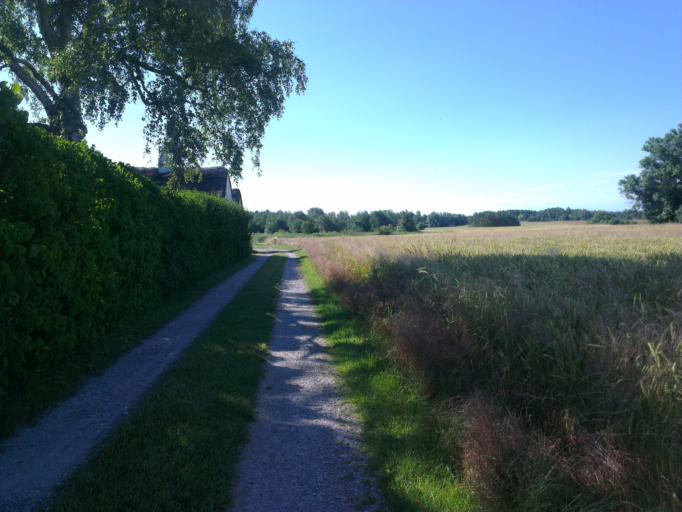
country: DK
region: Capital Region
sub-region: Frederikssund Kommune
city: Frederikssund
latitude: 55.7963
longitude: 12.0412
